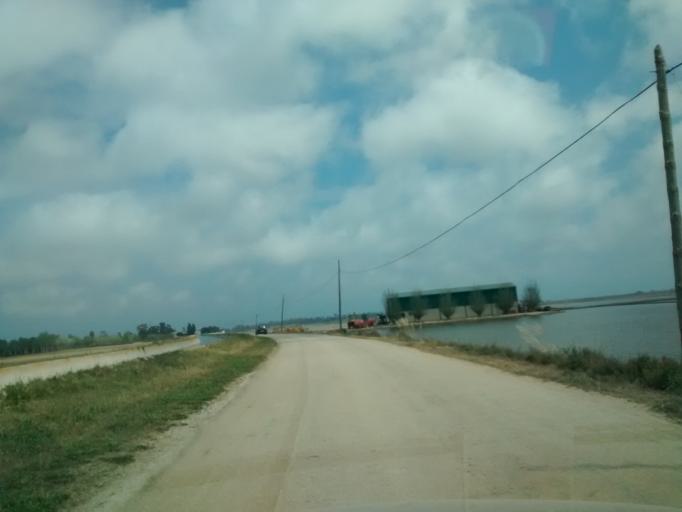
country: ES
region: Catalonia
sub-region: Provincia de Tarragona
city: Deltebre
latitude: 40.6941
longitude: 0.8021
